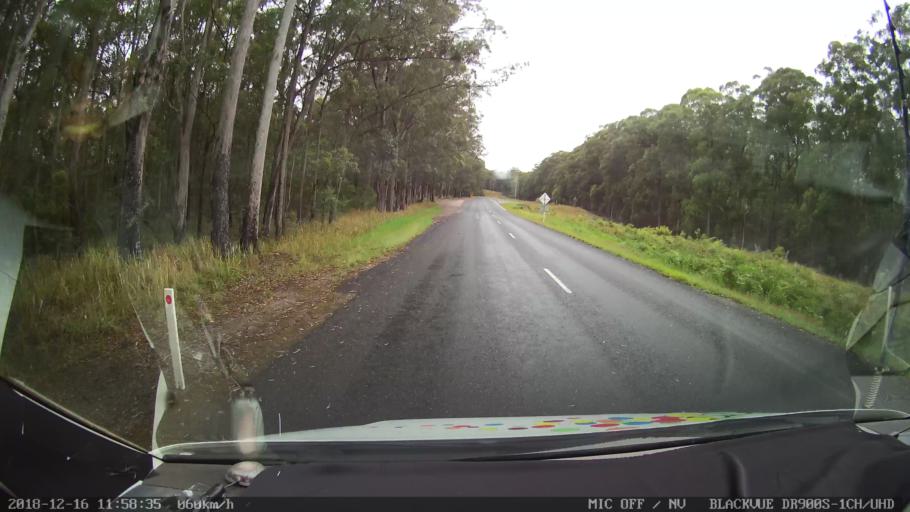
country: AU
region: New South Wales
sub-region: Tenterfield Municipality
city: Carrolls Creek
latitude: -28.9234
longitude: 152.3137
